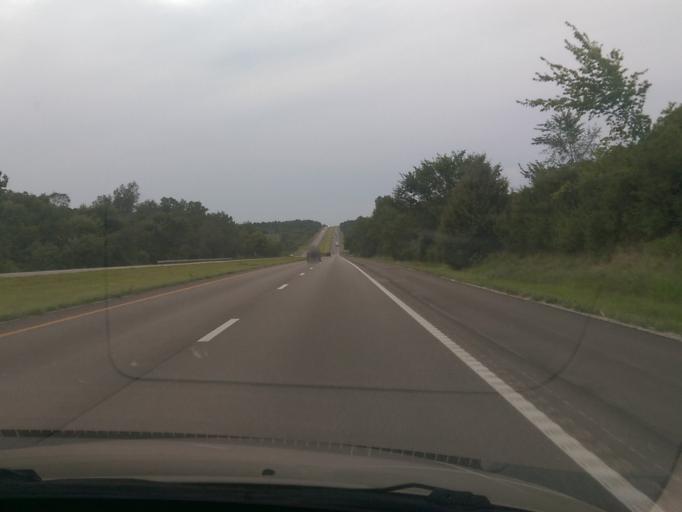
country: US
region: Missouri
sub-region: Andrew County
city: Savannah
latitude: 39.9333
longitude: -94.9270
